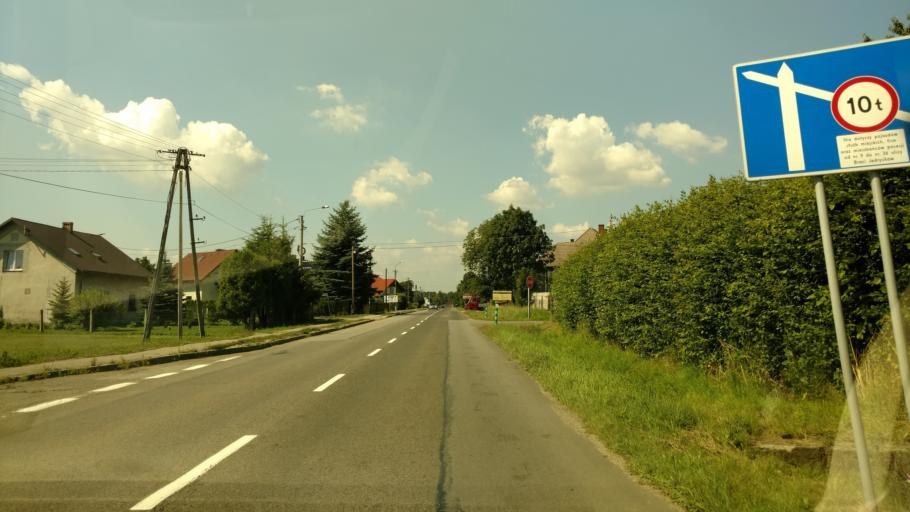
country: PL
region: Silesian Voivodeship
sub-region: Powiat pszczynski
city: Pszczyna
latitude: 49.9935
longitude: 18.9642
